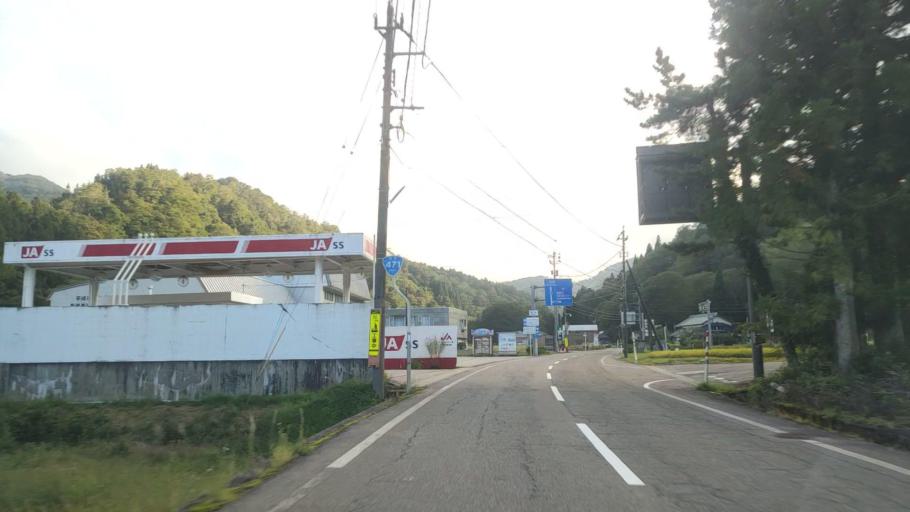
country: JP
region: Toyama
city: Yatsuomachi-higashikumisaka
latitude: 36.4533
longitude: 137.0410
